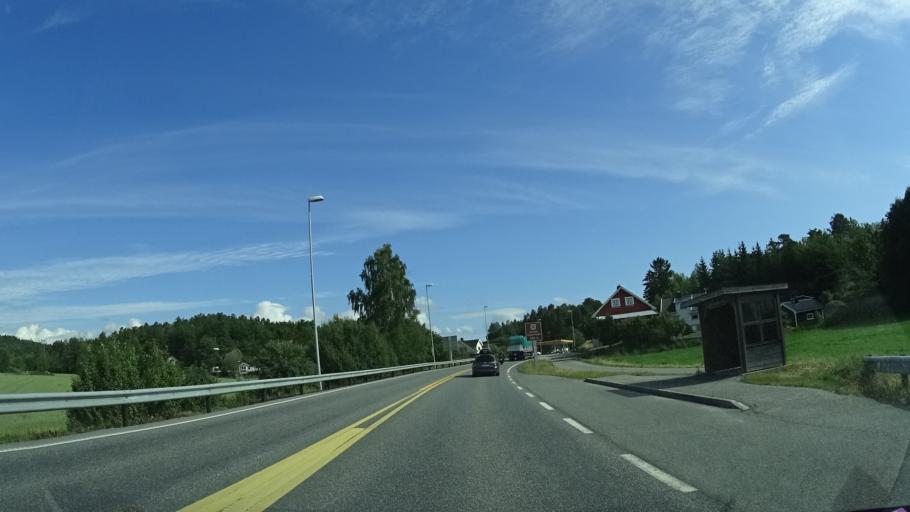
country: NO
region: Telemark
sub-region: Bamble
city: Langesund
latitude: 59.0107
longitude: 9.6641
